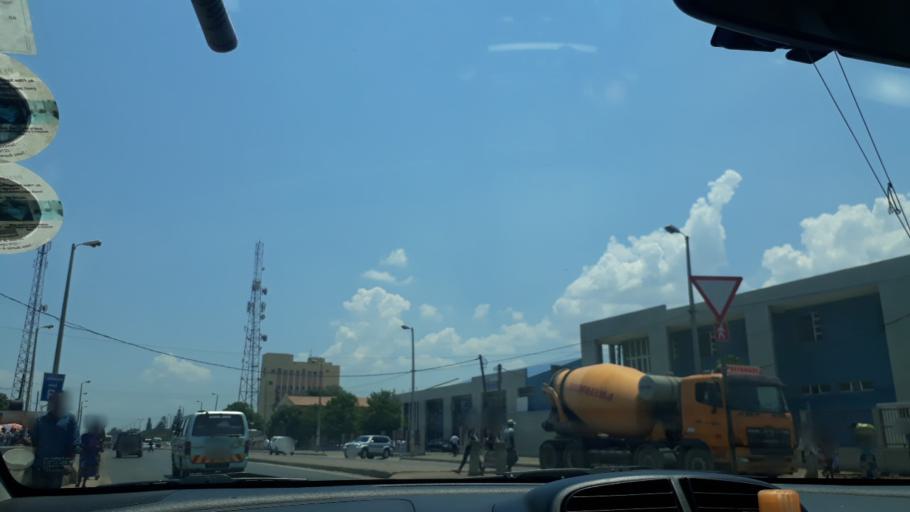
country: MZ
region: Maputo City
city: Maputo
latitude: -25.9350
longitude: 32.5501
